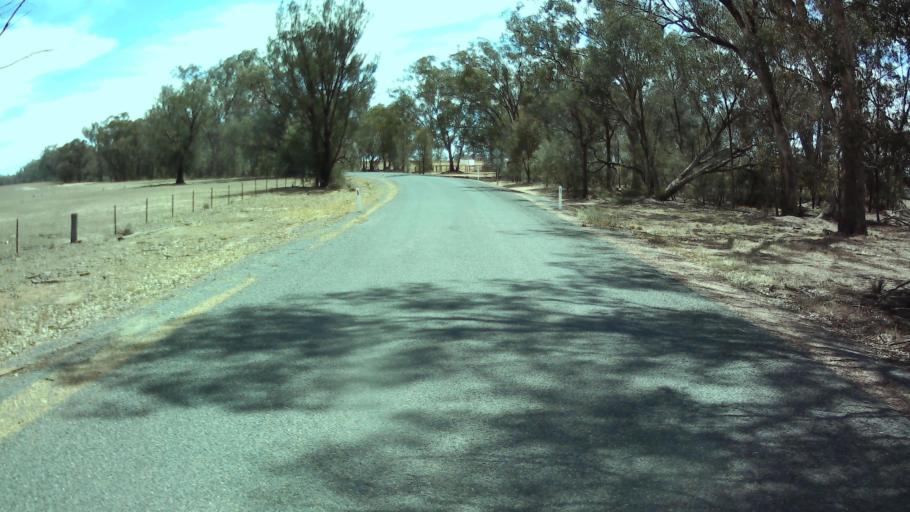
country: AU
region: New South Wales
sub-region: Weddin
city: Grenfell
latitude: -33.7389
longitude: 148.2090
